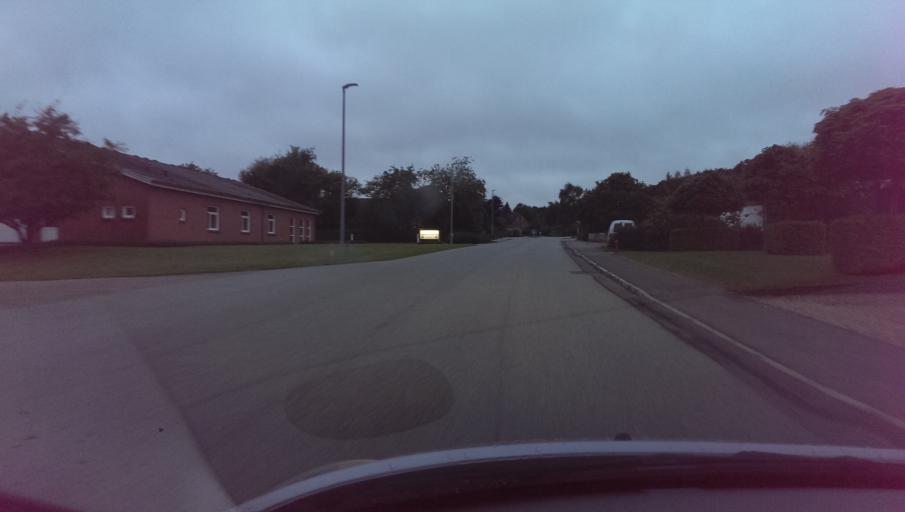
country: DK
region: South Denmark
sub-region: Varde Kommune
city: Olgod
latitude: 55.8146
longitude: 8.6290
